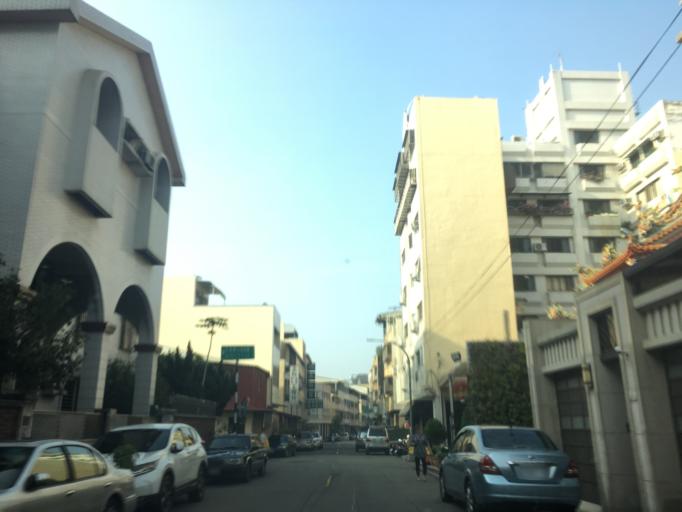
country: TW
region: Taiwan
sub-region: Taichung City
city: Taichung
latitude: 24.1703
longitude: 120.6885
